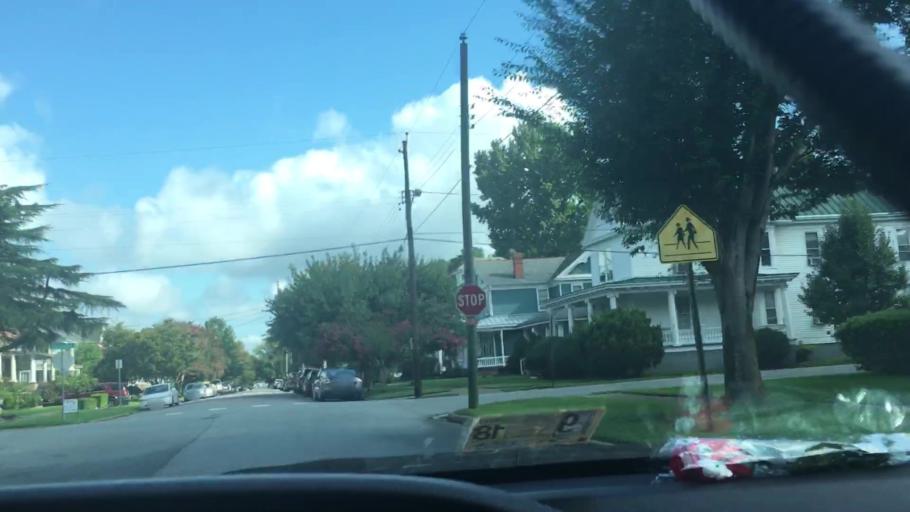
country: US
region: Virginia
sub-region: City of Portsmouth
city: Portsmouth Heights
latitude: 36.8480
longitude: -76.3379
